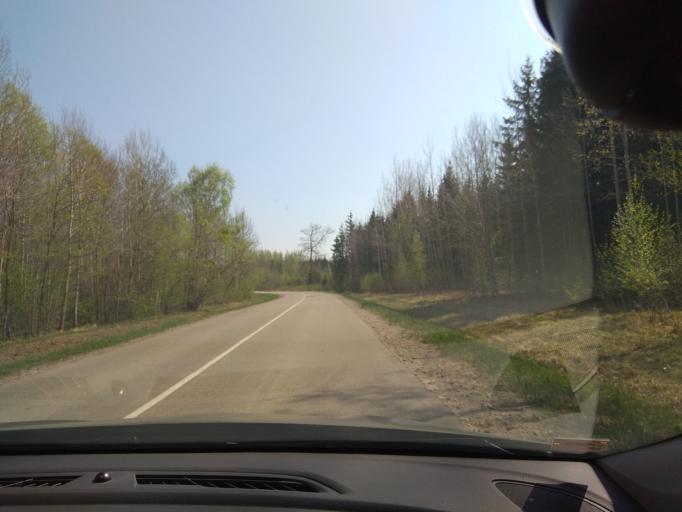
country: LT
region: Panevezys
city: Pasvalys
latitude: 55.9753
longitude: 24.1971
